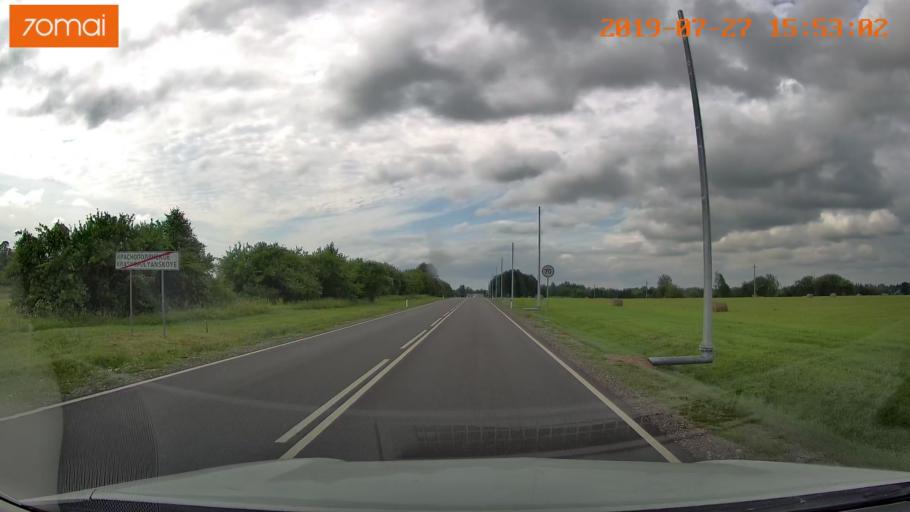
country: RU
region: Kaliningrad
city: Chernyakhovsk
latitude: 54.6021
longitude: 21.9602
